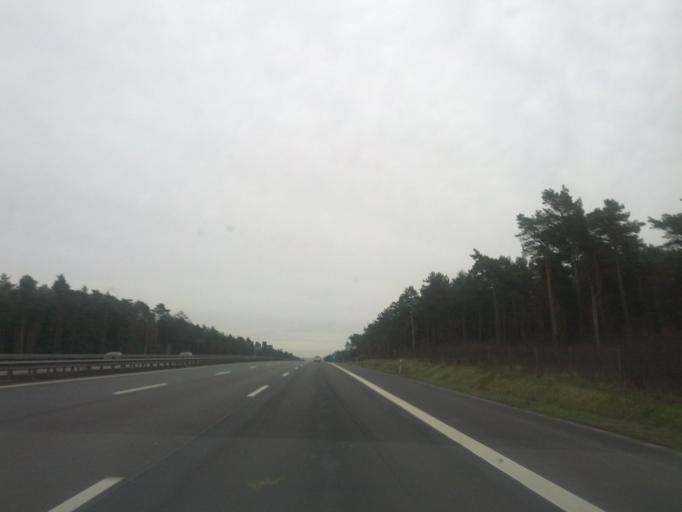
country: DE
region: Lower Saxony
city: Heidenau
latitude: 53.3405
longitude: 9.6453
